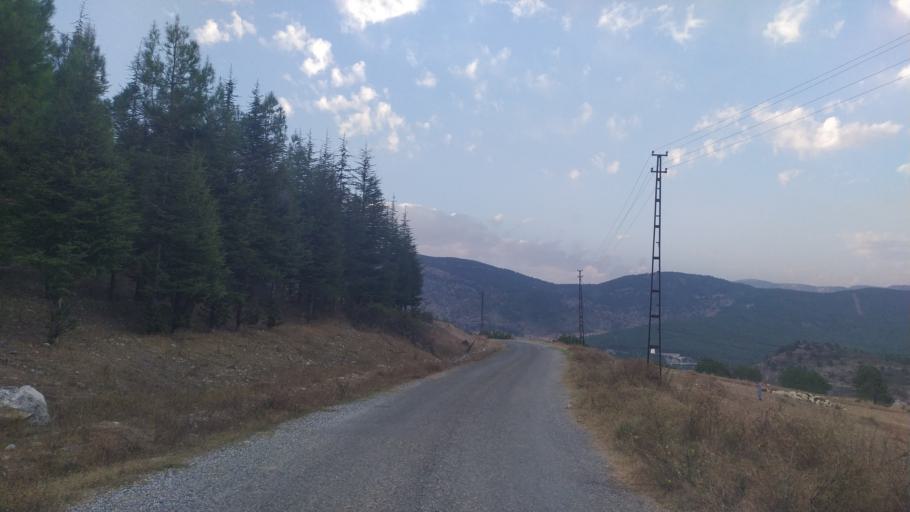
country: TR
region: Mersin
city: Camliyayla
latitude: 37.2264
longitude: 34.7102
